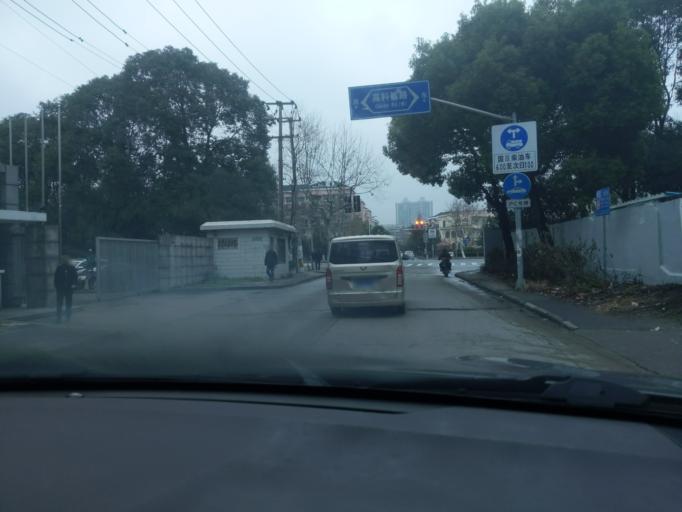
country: CN
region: Shanghai Shi
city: Huamu
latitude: 31.1888
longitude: 121.5250
